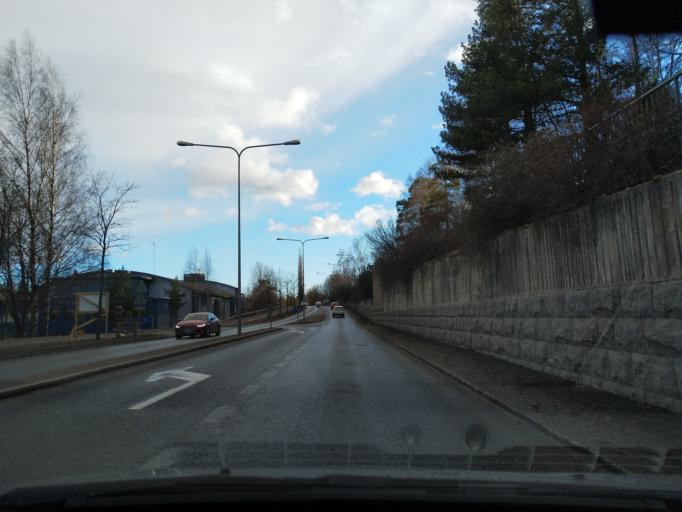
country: FI
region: Uusimaa
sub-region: Helsinki
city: Vantaa
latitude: 60.2739
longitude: 25.0764
